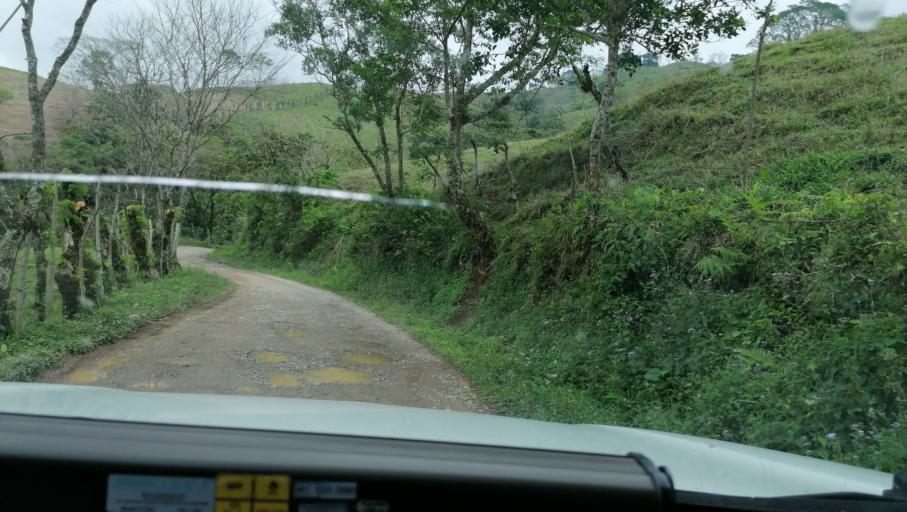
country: MX
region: Chiapas
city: Ocotepec
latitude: 17.3252
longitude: -93.1334
